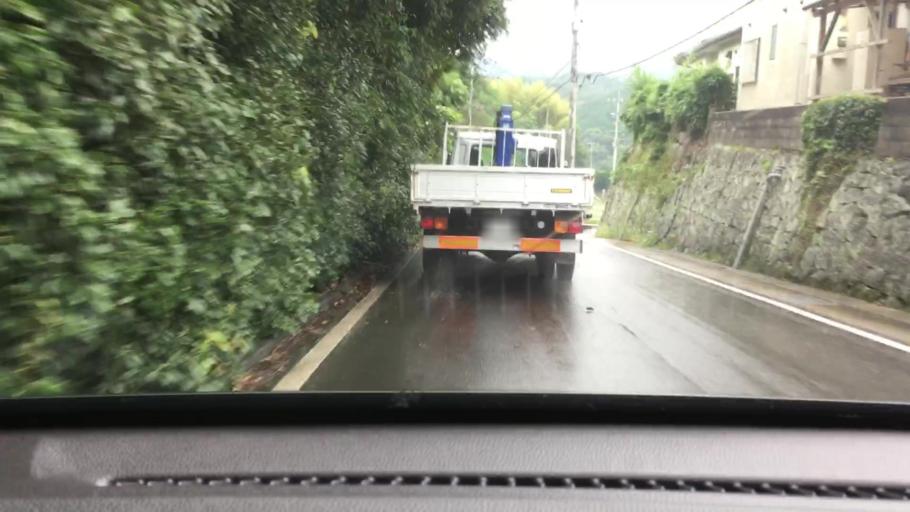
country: JP
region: Nagasaki
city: Togitsu
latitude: 32.8572
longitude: 129.7789
